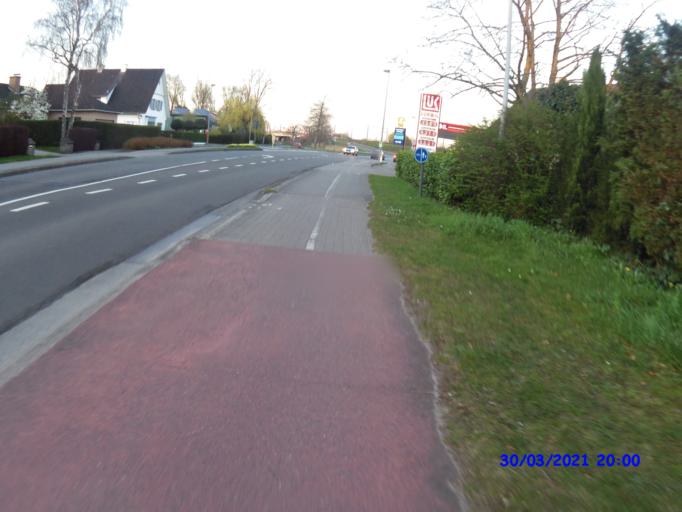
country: BE
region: Flanders
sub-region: Provincie Oost-Vlaanderen
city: Gent
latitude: 51.0318
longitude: 3.6844
